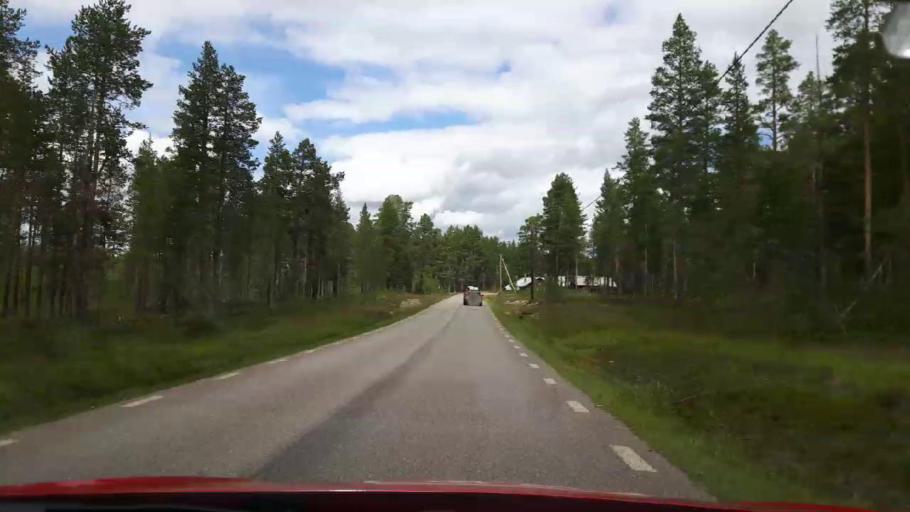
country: NO
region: Hedmark
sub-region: Trysil
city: Innbygda
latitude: 61.8308
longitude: 12.9523
